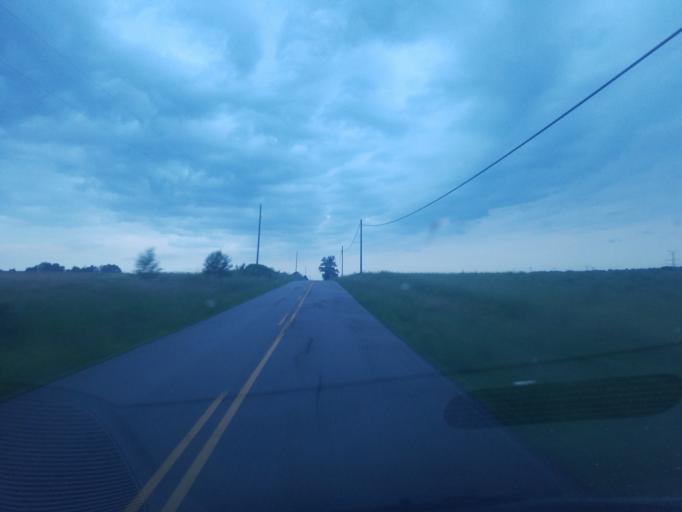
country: US
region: Ohio
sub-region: Mahoning County
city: Canfield
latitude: 40.9726
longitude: -80.7569
